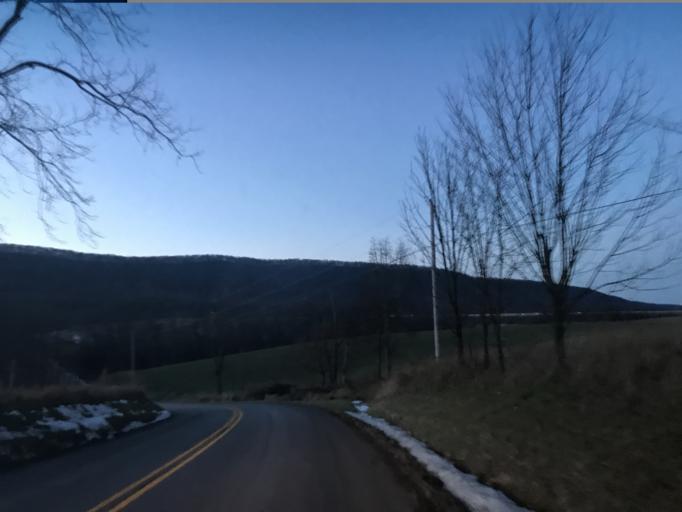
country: US
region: Pennsylvania
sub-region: Fulton County
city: McConnellsburg
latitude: 40.0537
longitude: -78.0868
